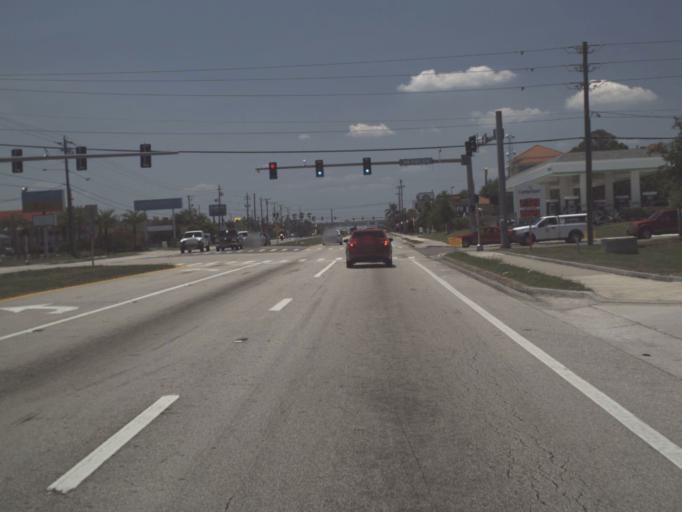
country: US
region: Florida
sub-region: Brevard County
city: June Park
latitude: 28.0790
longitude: -80.6995
